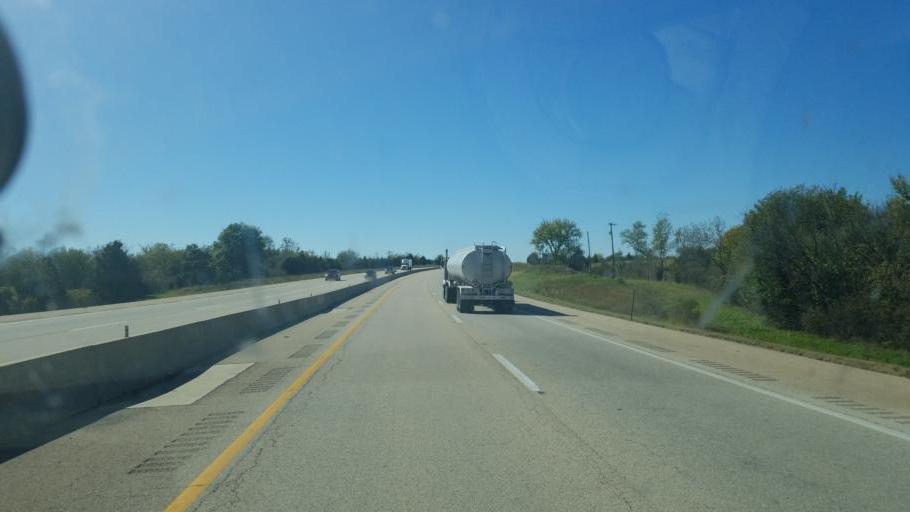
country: US
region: Kansas
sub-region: Douglas County
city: Eudora
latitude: 39.0125
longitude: -95.1485
